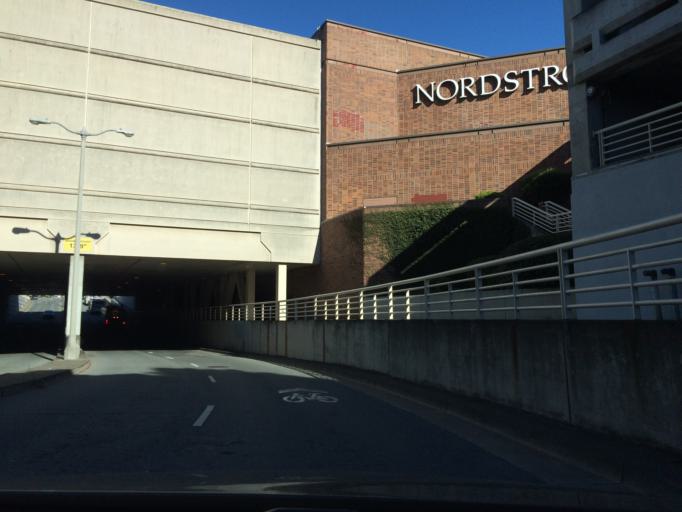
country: US
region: California
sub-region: San Mateo County
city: Daly City
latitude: 37.7271
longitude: -122.4783
